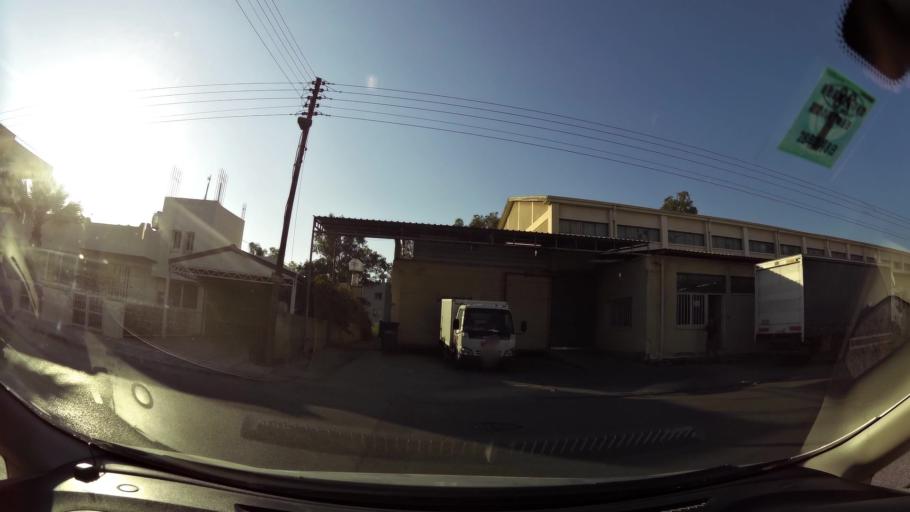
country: CY
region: Lefkosia
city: Nicosia
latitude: 35.1990
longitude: 33.3469
